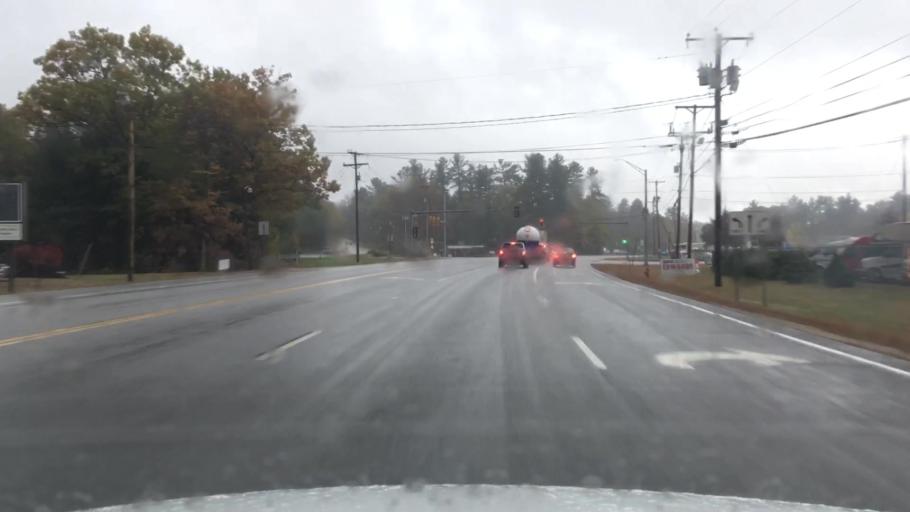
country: US
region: New Hampshire
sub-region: Strafford County
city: Rochester
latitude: 43.2552
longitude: -70.9791
